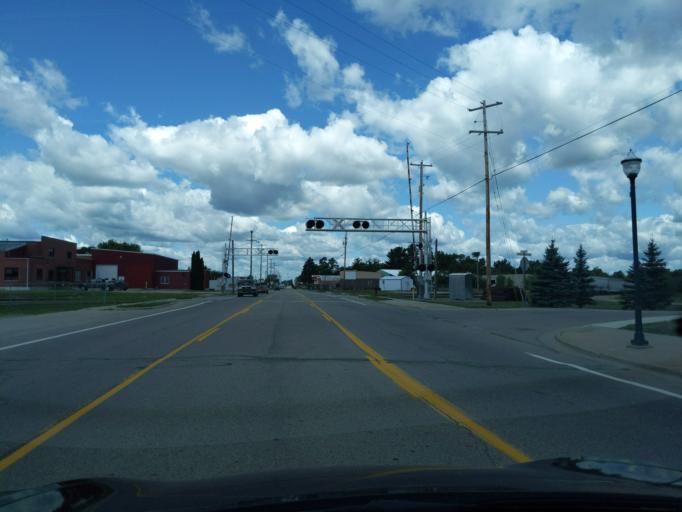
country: US
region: Michigan
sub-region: Clare County
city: Clare
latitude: 43.8197
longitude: -84.7736
